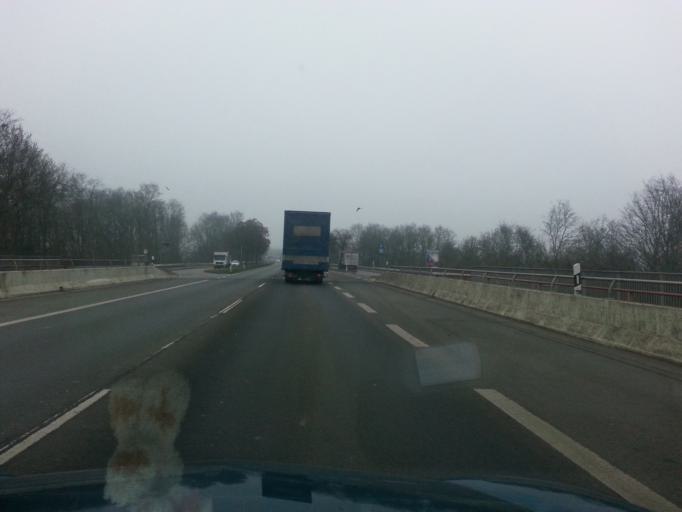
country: DE
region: North Rhine-Westphalia
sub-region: Regierungsbezirk Dusseldorf
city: Emmerich
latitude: 51.8326
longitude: 6.2267
